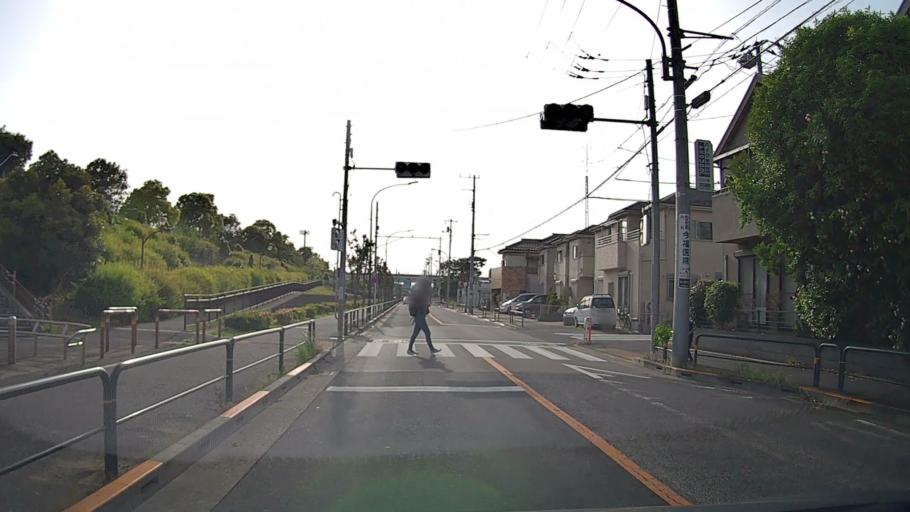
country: JP
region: Saitama
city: Soka
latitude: 35.8013
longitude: 139.7741
